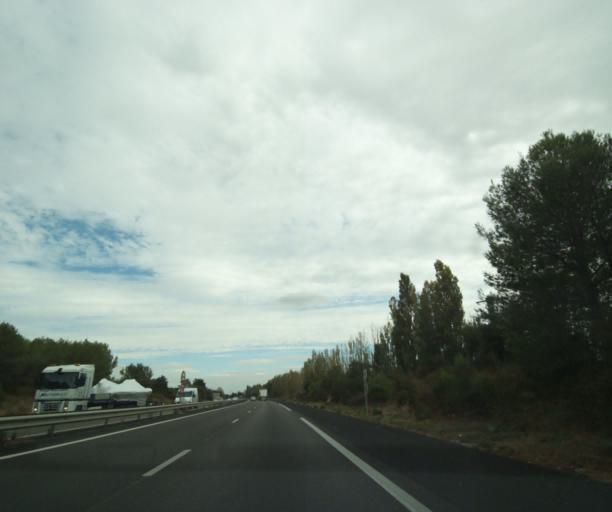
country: FR
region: Languedoc-Roussillon
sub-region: Departement du Gard
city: Garons
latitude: 43.7431
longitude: 4.4443
